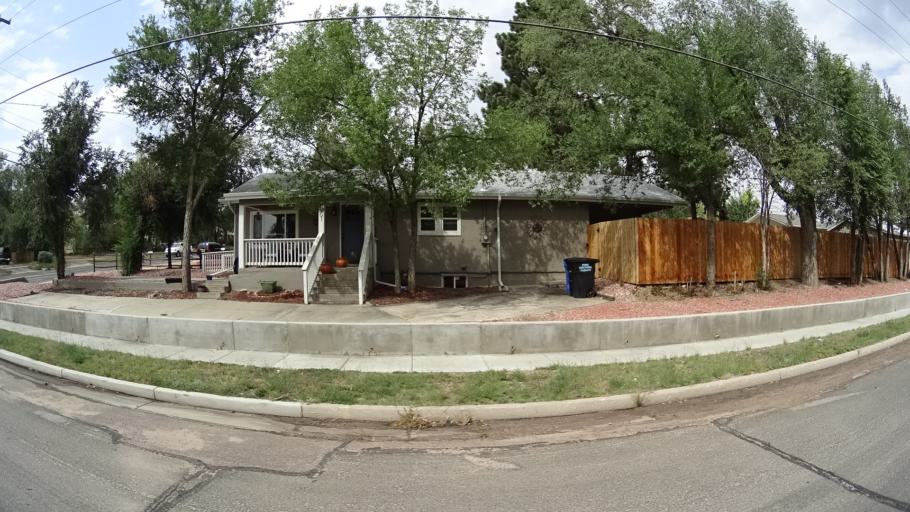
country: US
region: Colorado
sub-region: El Paso County
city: Colorado Springs
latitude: 38.8450
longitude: -104.7853
